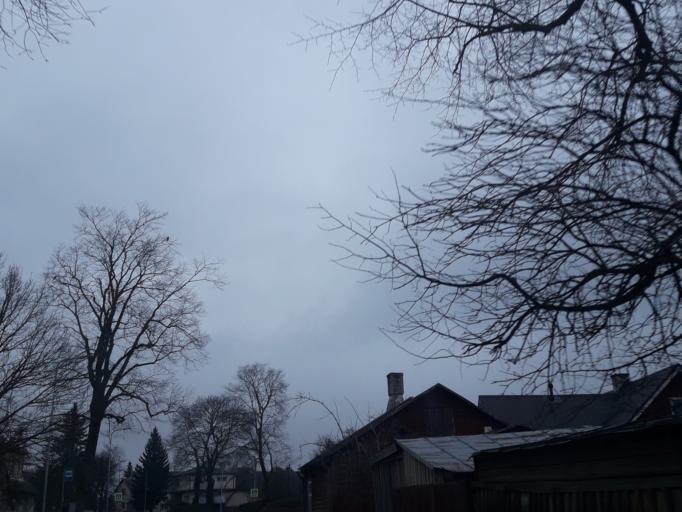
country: EE
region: Saare
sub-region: Kuressaare linn
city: Kuressaare
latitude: 58.2524
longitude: 22.4755
